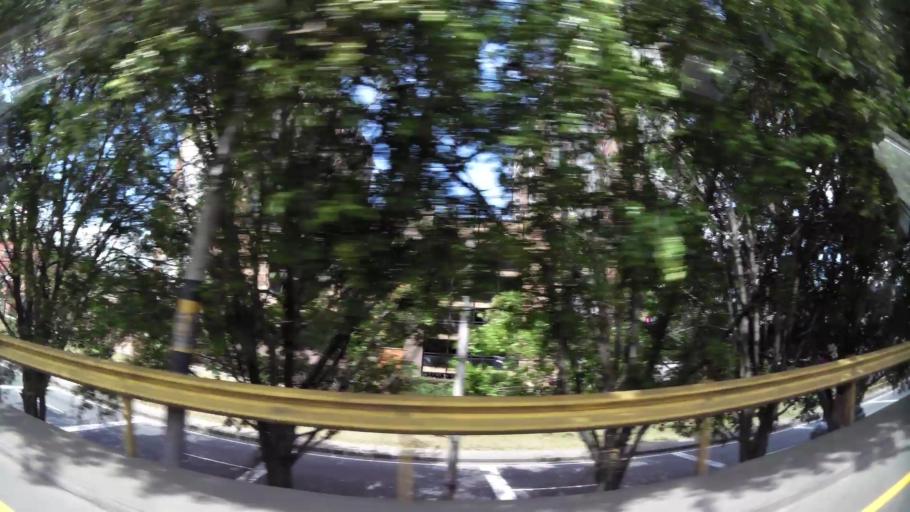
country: CO
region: Antioquia
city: Bello
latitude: 6.3160
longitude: -75.5556
